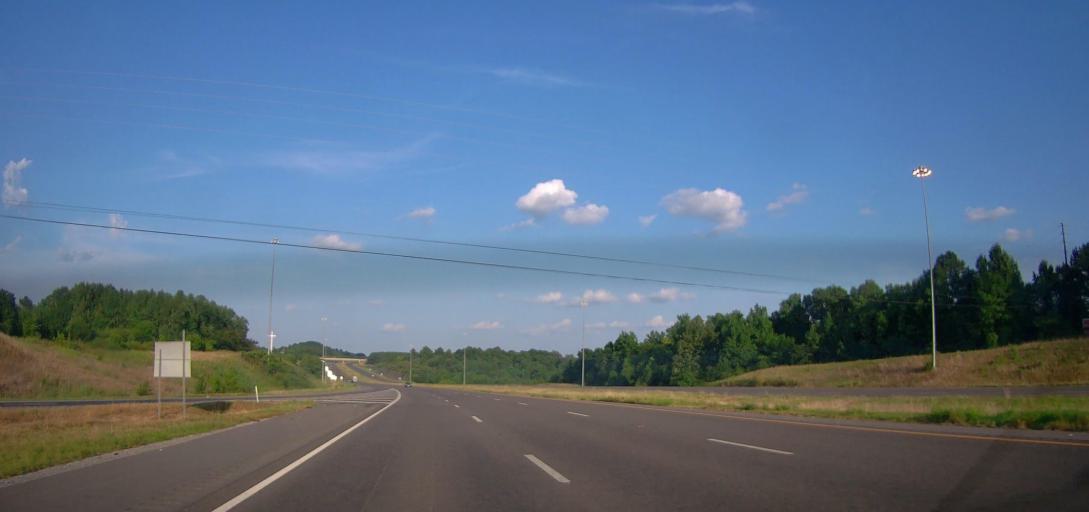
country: US
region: Alabama
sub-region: Walker County
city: Jasper
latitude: 33.7923
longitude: -87.2360
